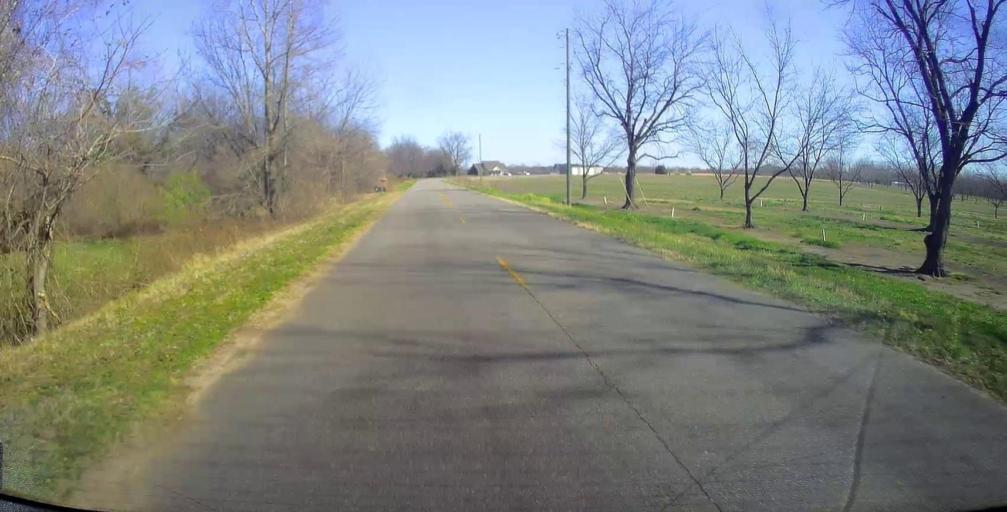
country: US
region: Georgia
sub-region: Peach County
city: Byron
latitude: 32.6293
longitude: -83.8429
